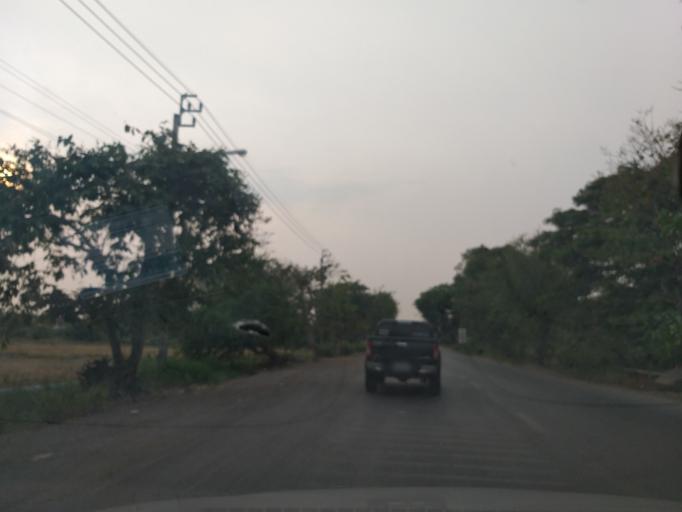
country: TH
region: Bangkok
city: Nong Chok
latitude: 13.8436
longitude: 100.8987
